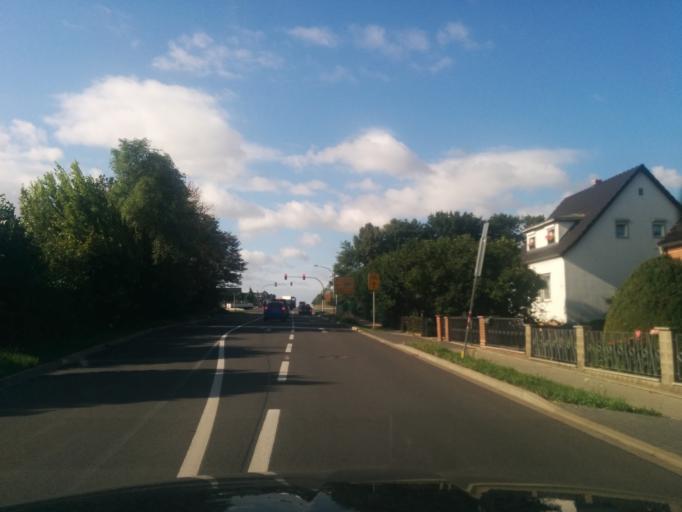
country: DE
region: Saxony-Anhalt
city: Bennstedt
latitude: 51.4779
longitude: 11.8240
